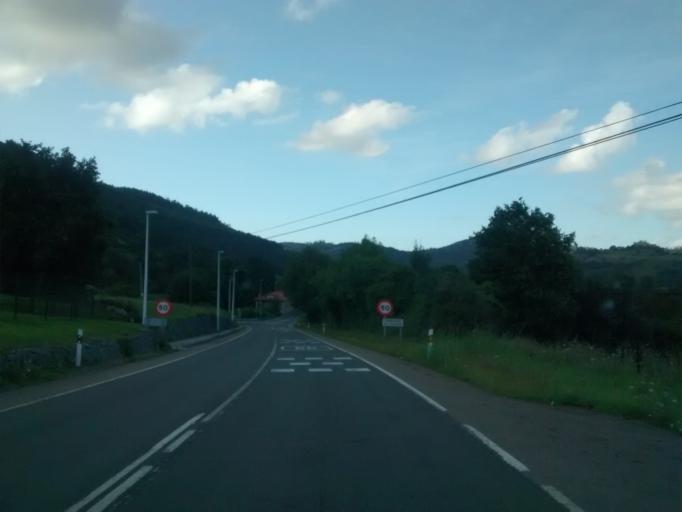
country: ES
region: Cantabria
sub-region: Provincia de Cantabria
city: Corvera
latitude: 43.2630
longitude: -3.9474
